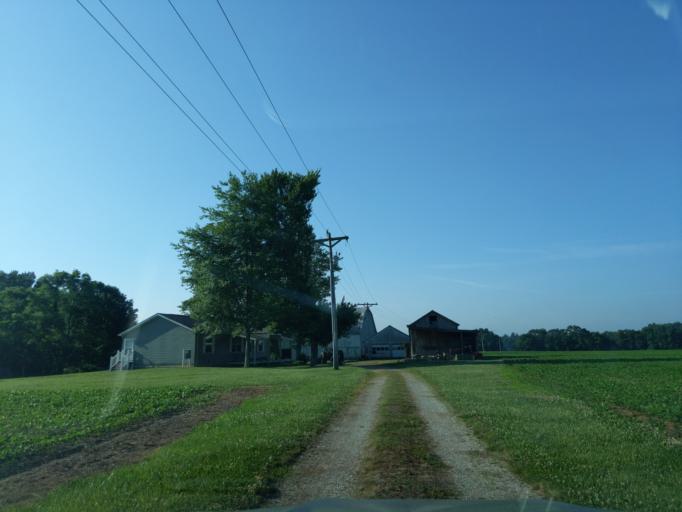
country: US
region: Indiana
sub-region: Decatur County
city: Westport
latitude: 39.1973
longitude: -85.4345
